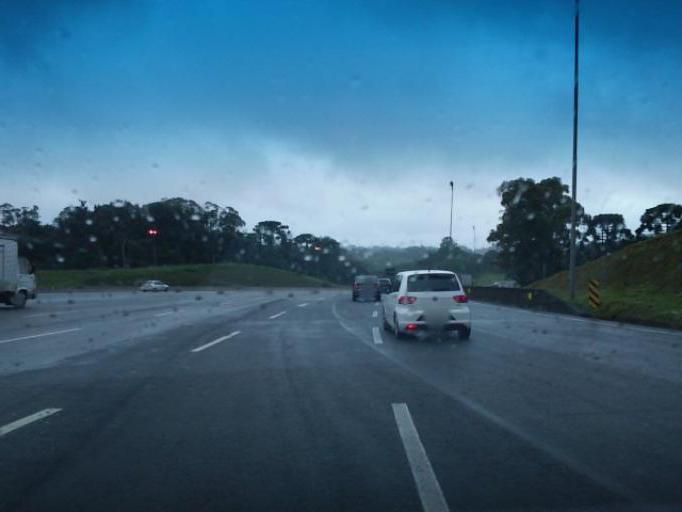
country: BR
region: Parana
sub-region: Sao Jose Dos Pinhais
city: Sao Jose dos Pinhais
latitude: -25.7466
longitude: -49.1295
